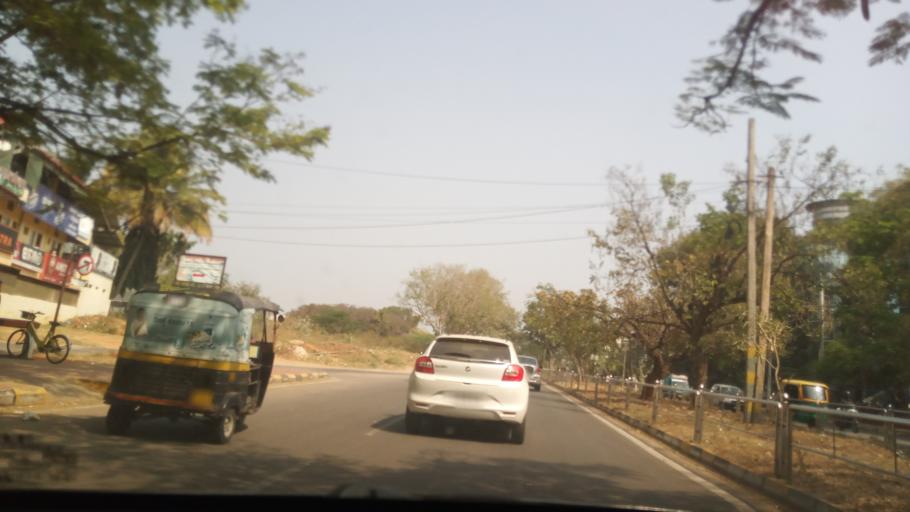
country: IN
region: Karnataka
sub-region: Mysore
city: Mysore
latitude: 12.3024
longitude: 76.6265
